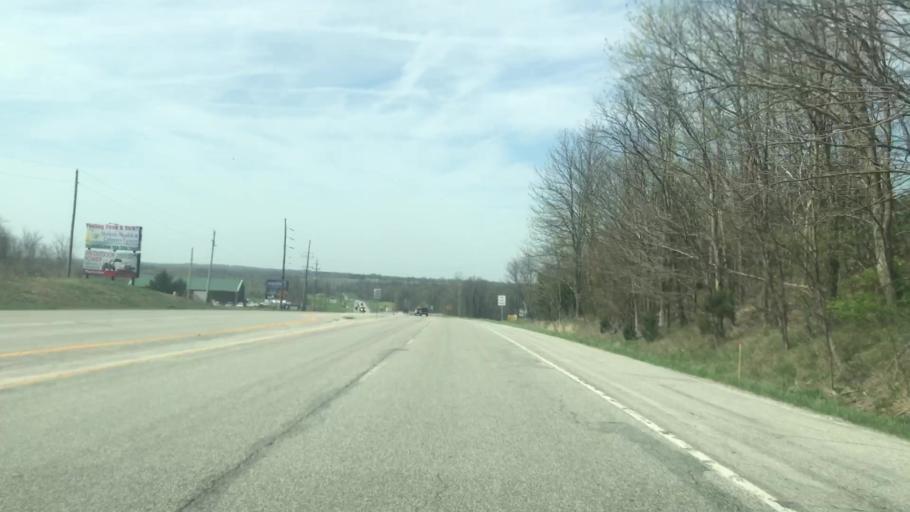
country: US
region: Indiana
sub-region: Putnam County
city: Cloverdale
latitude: 39.5371
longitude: -86.8035
